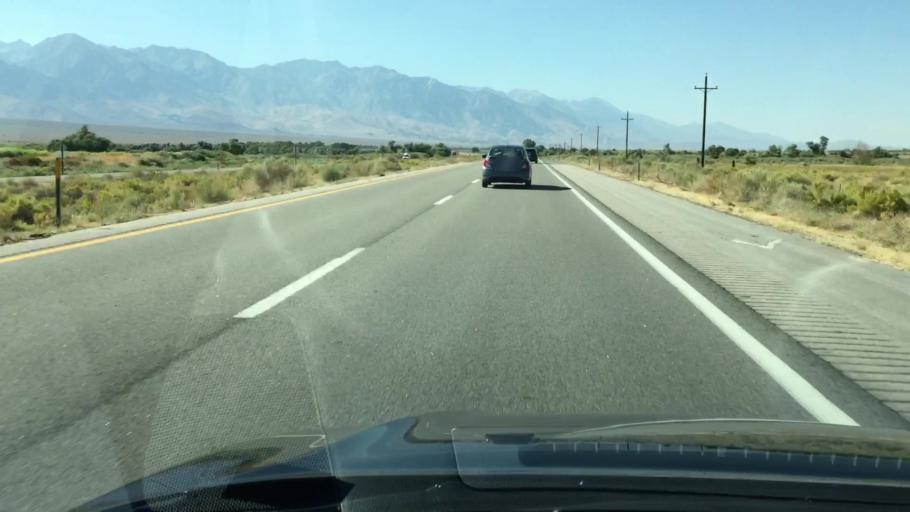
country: US
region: California
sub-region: Inyo County
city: Lone Pine
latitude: 36.6984
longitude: -118.1196
